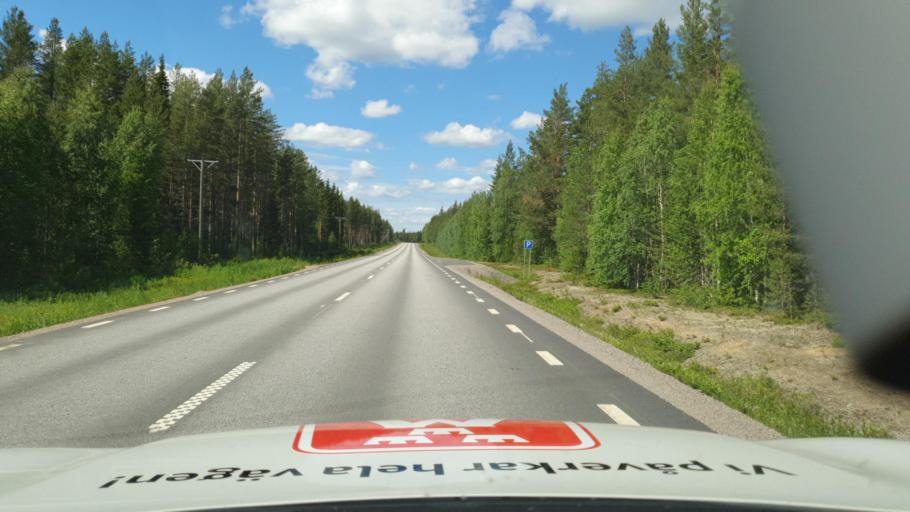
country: SE
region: Vaesterbotten
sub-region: Skelleftea Kommun
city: Boliden
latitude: 64.9308
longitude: 20.3099
